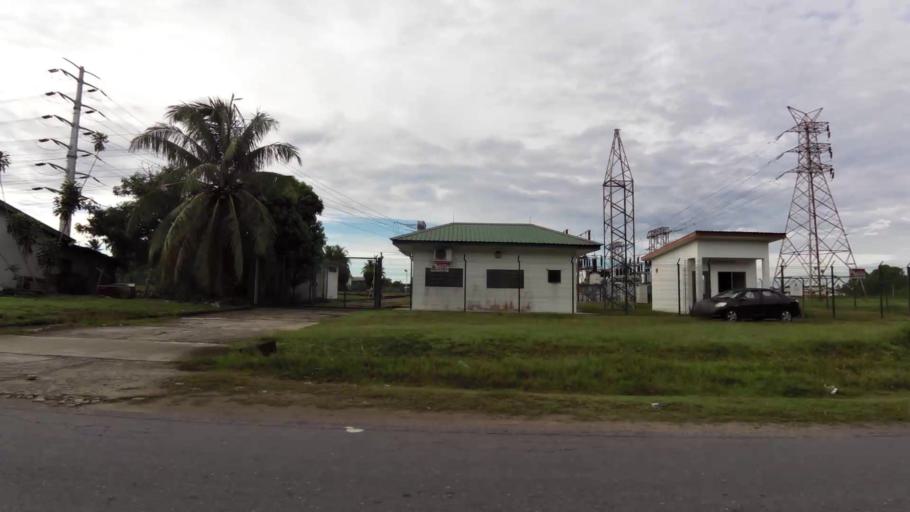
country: BN
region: Belait
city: Seria
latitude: 4.6151
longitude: 114.3399
